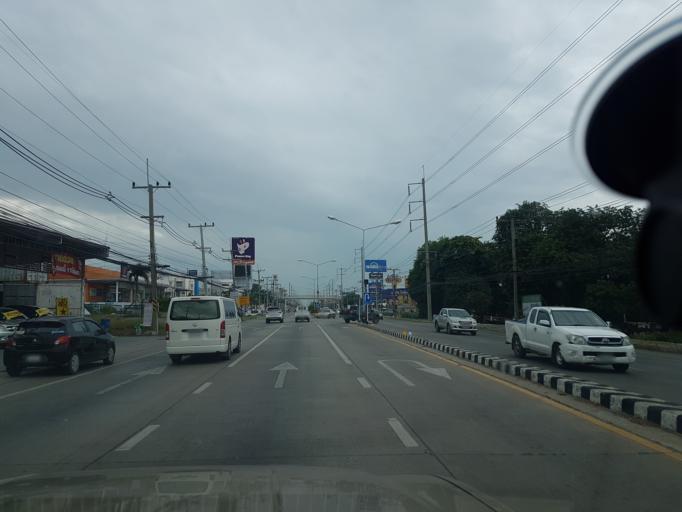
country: TH
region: Lop Buri
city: Lop Buri
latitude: 14.7825
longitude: 100.6855
